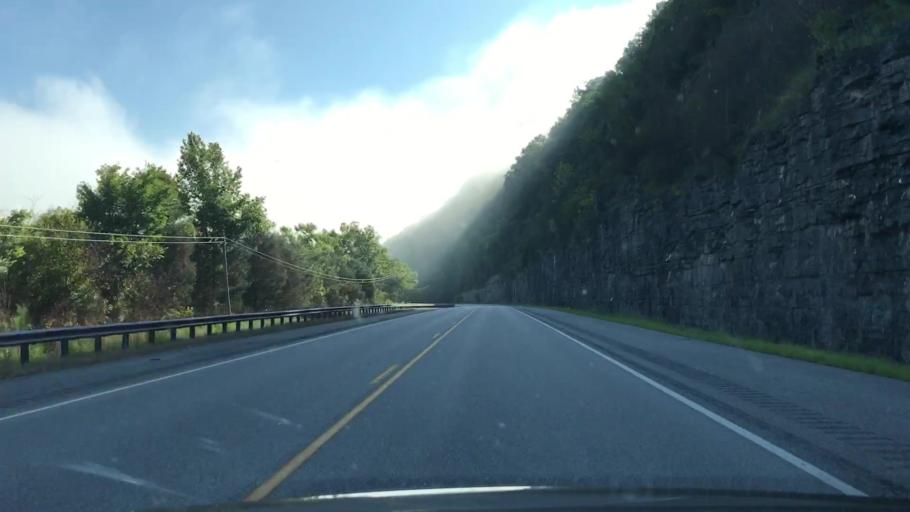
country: US
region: Tennessee
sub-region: Jackson County
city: Gainesboro
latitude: 36.4404
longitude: -85.5905
